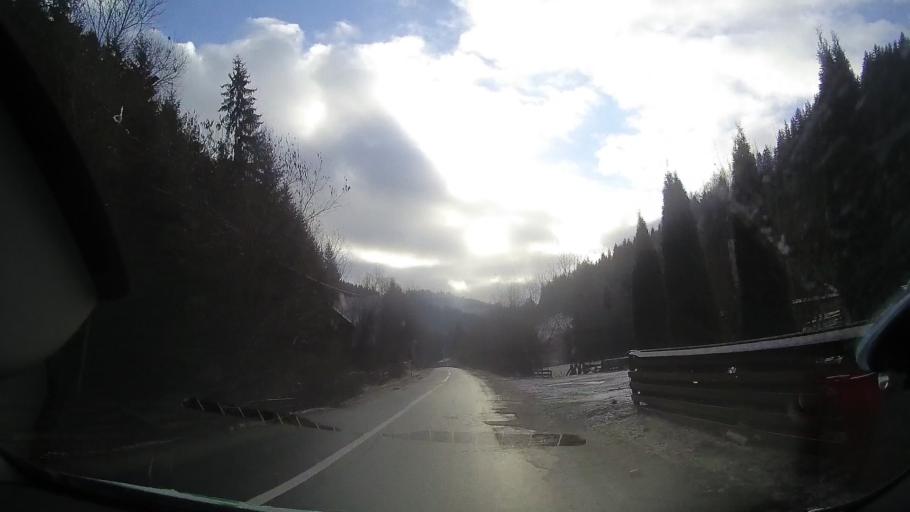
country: RO
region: Alba
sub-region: Comuna Horea
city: Horea
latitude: 46.4972
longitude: 22.9566
